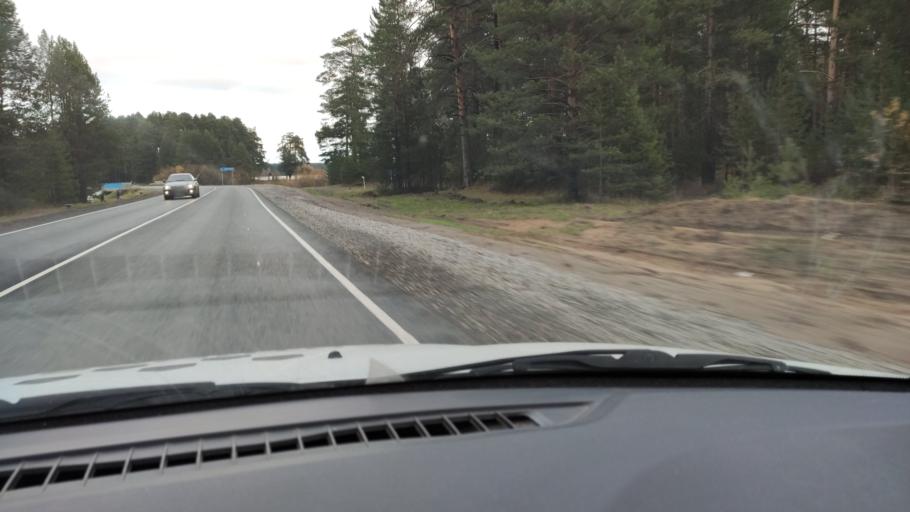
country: RU
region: Kirov
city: Belaya Kholunitsa
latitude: 58.8585
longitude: 50.8412
